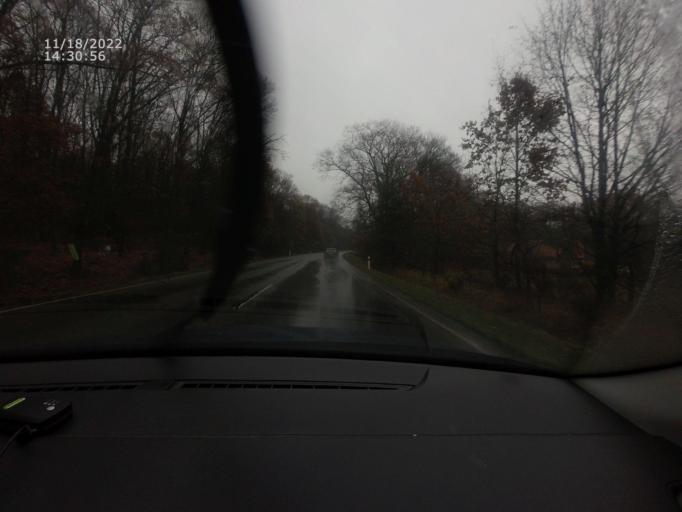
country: CZ
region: Jihocesky
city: Kovarov
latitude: 49.4504
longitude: 14.2553
